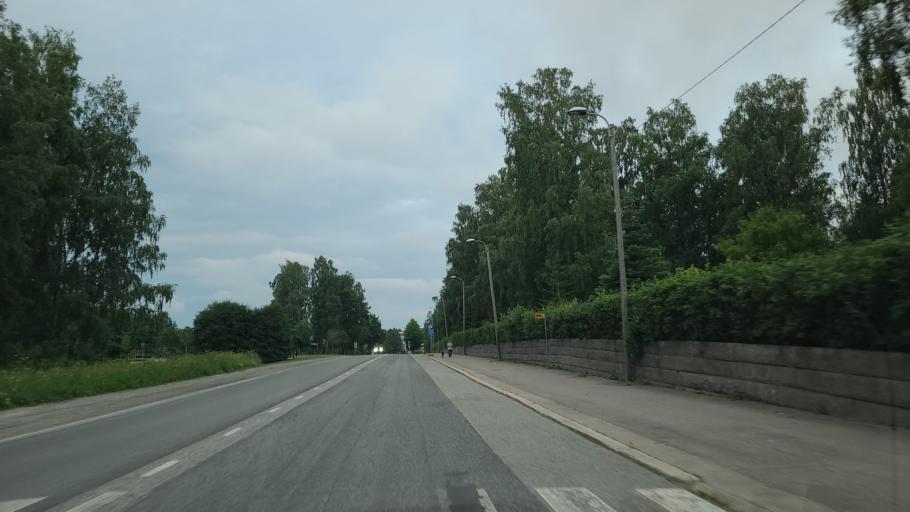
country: FI
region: Ostrobothnia
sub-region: Vaasa
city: Vaasa
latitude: 63.1095
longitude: 21.6184
